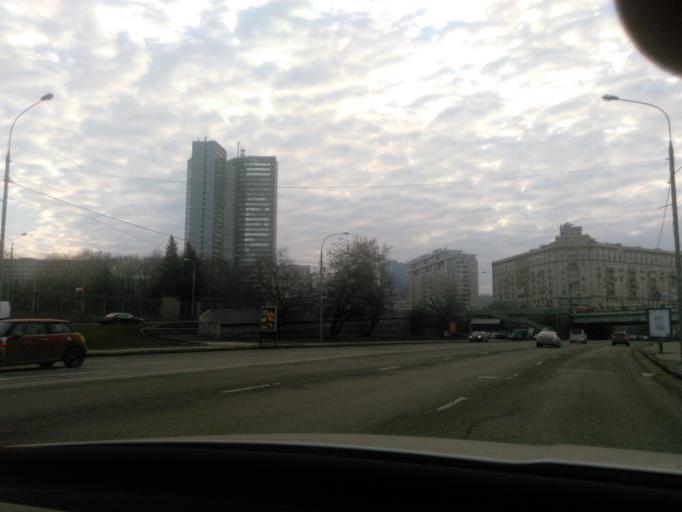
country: RU
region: Moskovskaya
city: Dorogomilovo
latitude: 55.7535
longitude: 37.5713
